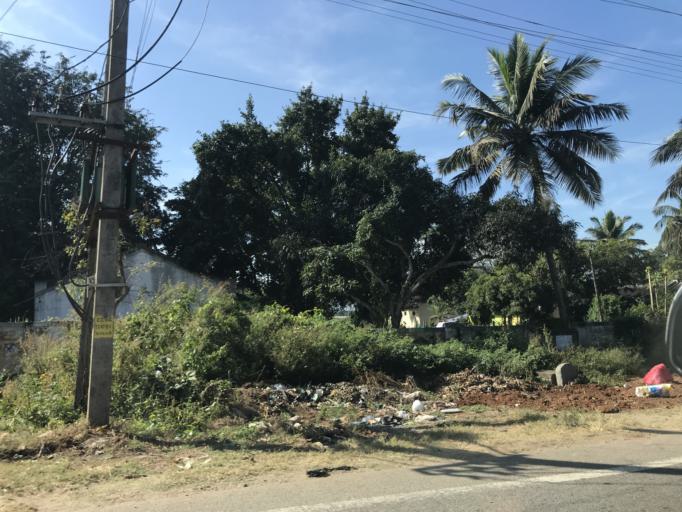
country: IN
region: Karnataka
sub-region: Mysore
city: Sargur
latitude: 12.1216
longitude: 76.4795
